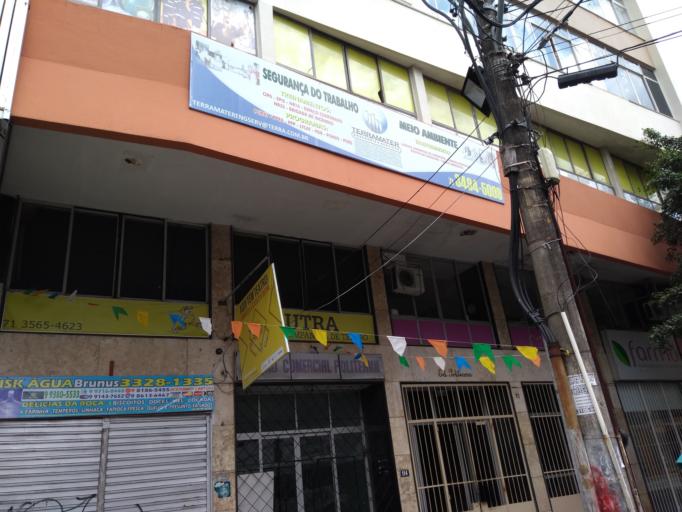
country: BR
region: Bahia
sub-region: Salvador
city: Salvador
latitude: -12.9865
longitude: -38.5193
